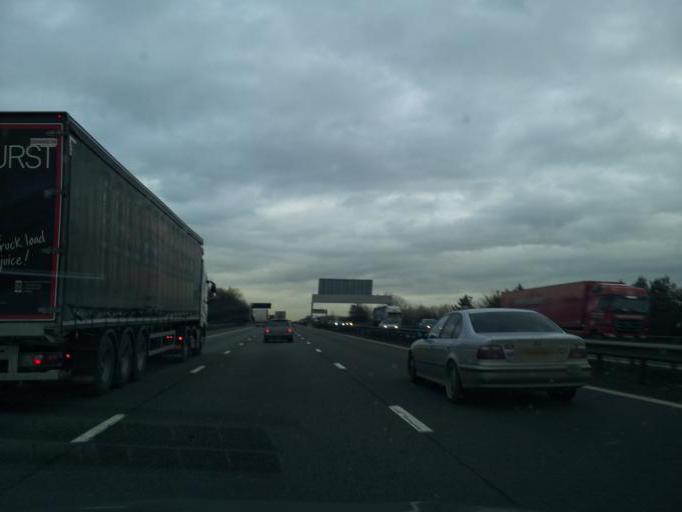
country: GB
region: England
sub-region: Warwickshire
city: Brandon
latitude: 52.4368
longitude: -1.3905
